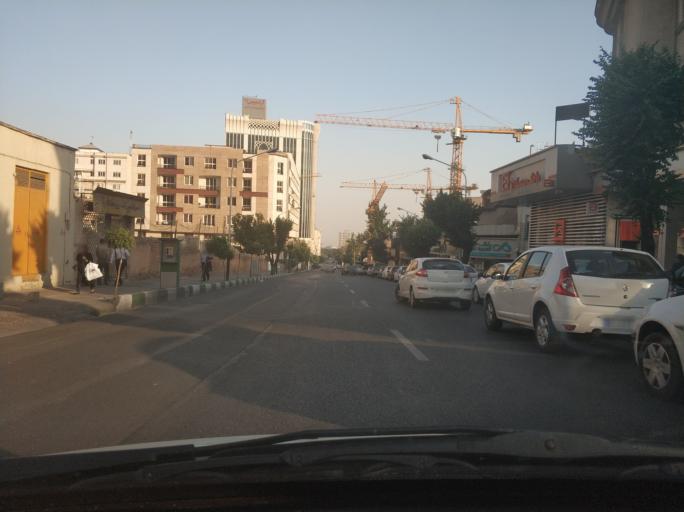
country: IR
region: Tehran
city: Tajrish
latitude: 35.7983
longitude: 51.4749
